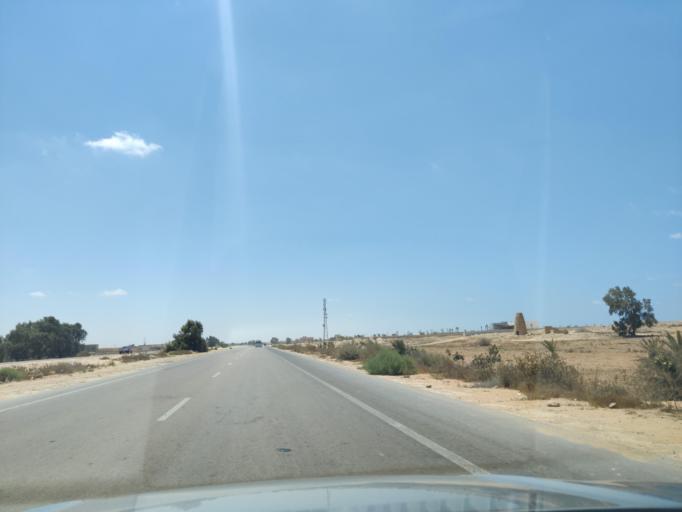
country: EG
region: Muhafazat Matruh
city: Al `Alamayn
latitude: 31.0698
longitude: 28.1414
